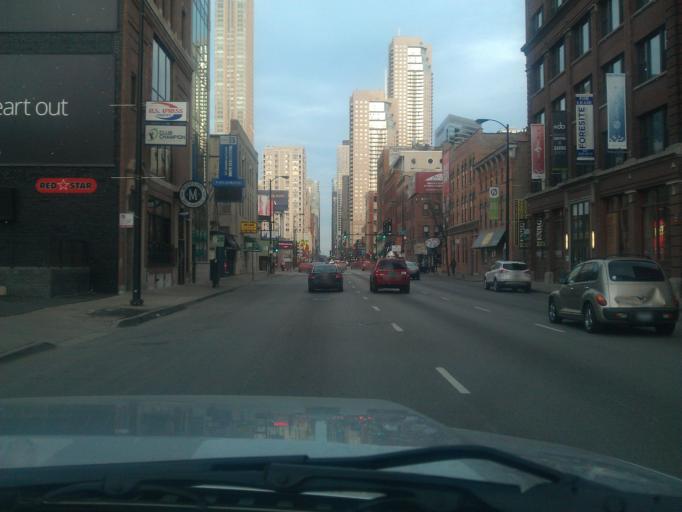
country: US
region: Illinois
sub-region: Cook County
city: Chicago
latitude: 41.8925
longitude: -87.6355
